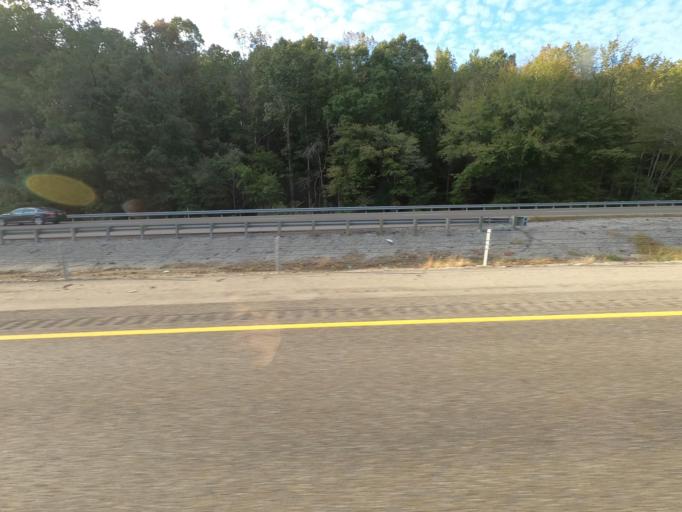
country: US
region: Tennessee
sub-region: Humphreys County
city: New Johnsonville
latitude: 35.8710
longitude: -87.8631
